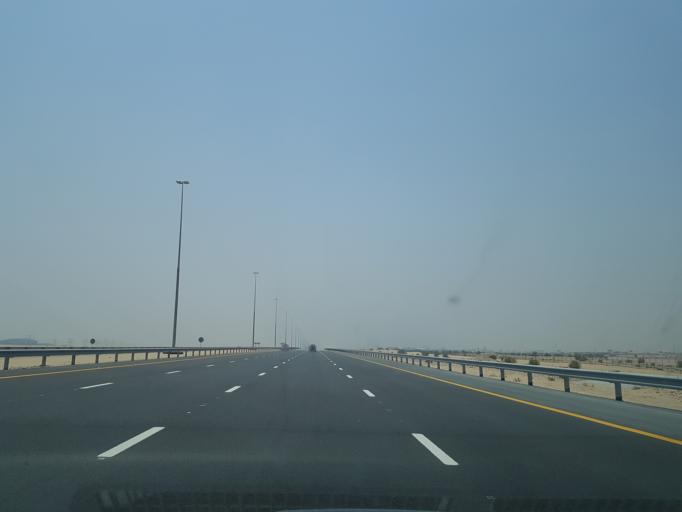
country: AE
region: Dubai
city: Dubai
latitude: 25.0782
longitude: 55.3346
